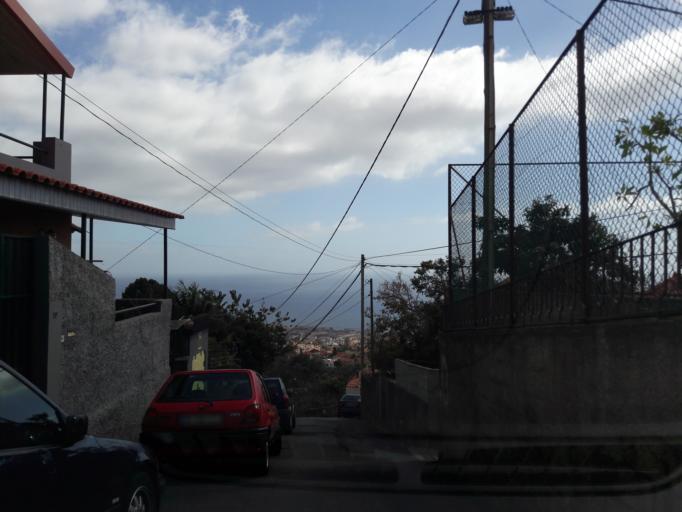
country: PT
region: Madeira
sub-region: Funchal
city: Nossa Senhora do Monte
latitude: 32.6647
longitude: -16.9133
